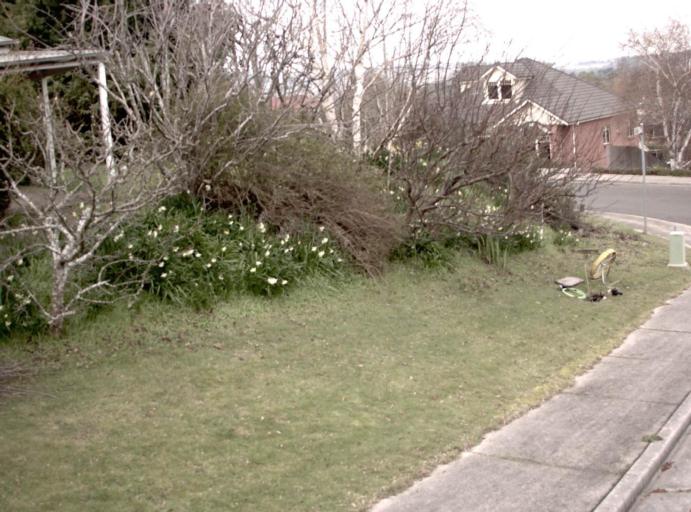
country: AU
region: Tasmania
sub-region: Launceston
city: Newstead
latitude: -41.4638
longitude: 147.1801
